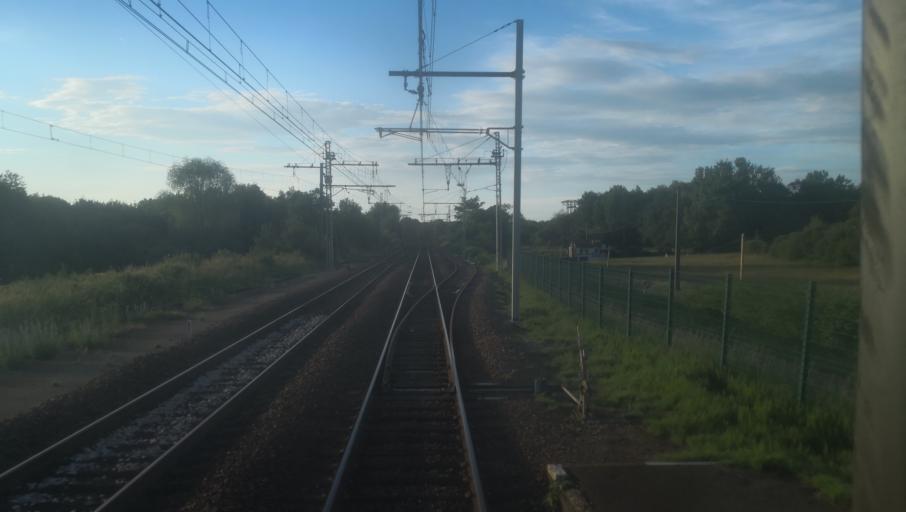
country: FR
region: Centre
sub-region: Departement de l'Indre
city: Chantome
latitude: 46.4414
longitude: 1.5523
